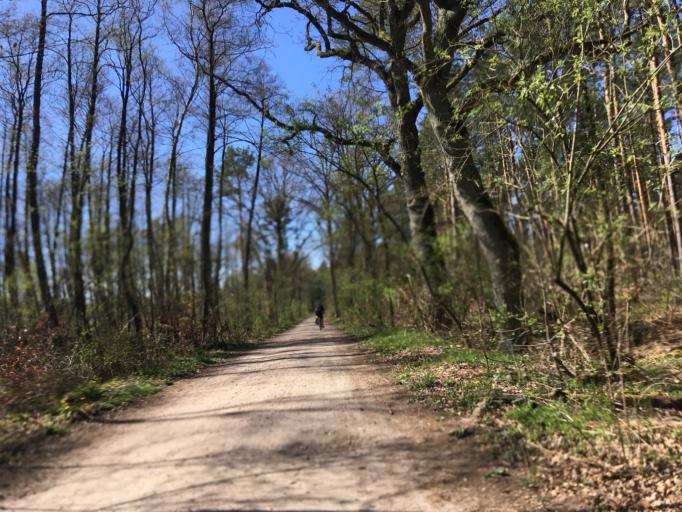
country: DE
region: Brandenburg
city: Wandlitz
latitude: 52.6898
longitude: 13.4642
